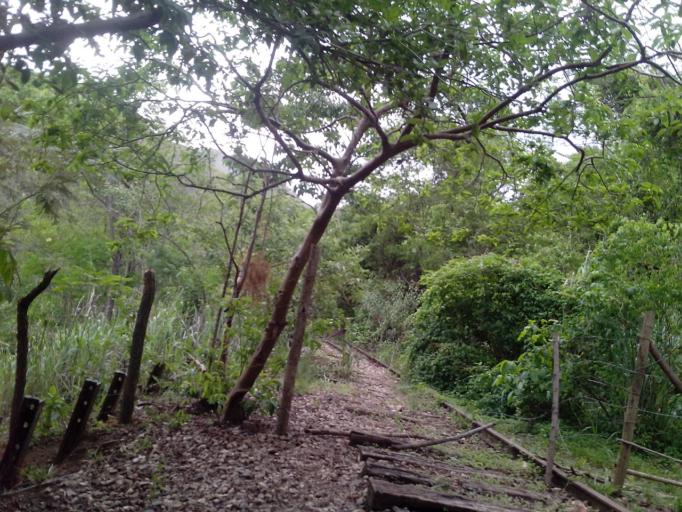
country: BR
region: Rio de Janeiro
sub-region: Miguel Pereira
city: Miguel Pereira
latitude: -22.5090
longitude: -43.5164
